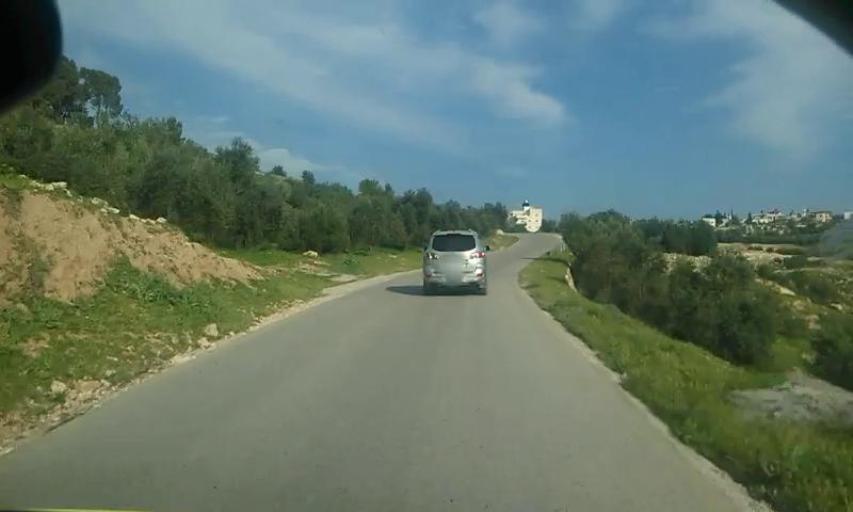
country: PS
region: West Bank
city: Nuba
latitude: 31.6146
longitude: 35.0211
